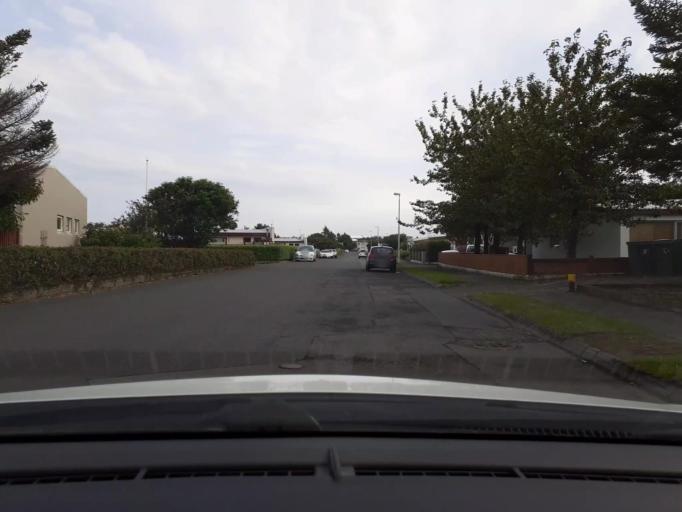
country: IS
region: Southern Peninsula
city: Reykjanesbaer
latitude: 63.9884
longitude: -22.5573
